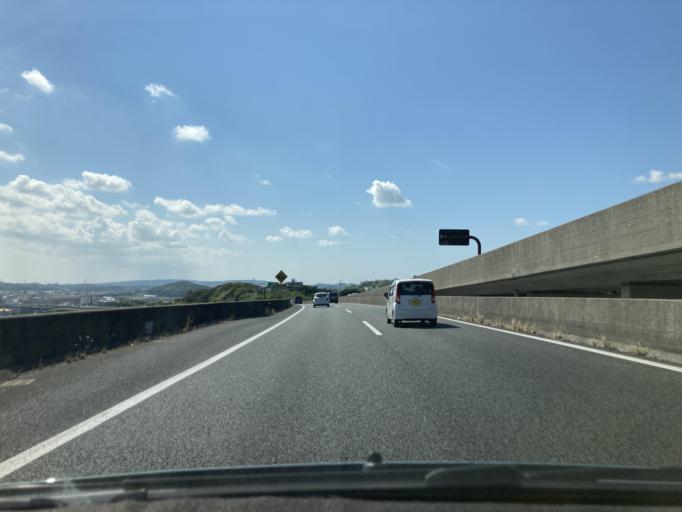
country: JP
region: Okinawa
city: Ginowan
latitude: 26.2133
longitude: 127.7384
